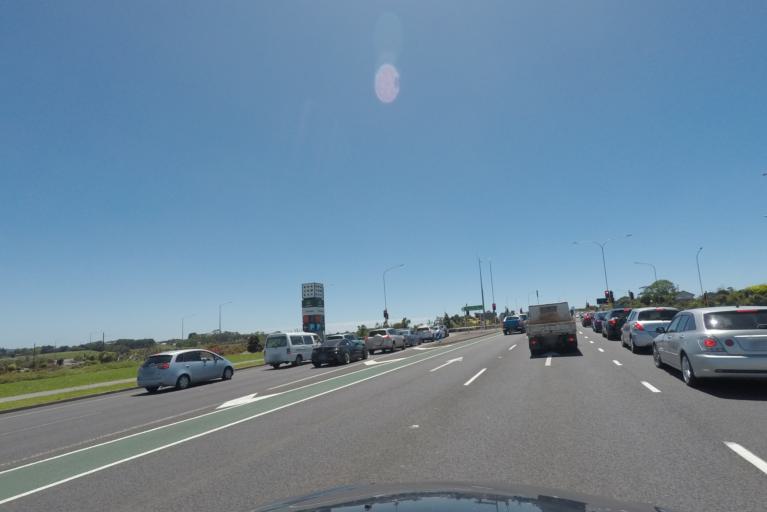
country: NZ
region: Auckland
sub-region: Auckland
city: Rosebank
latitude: -36.8194
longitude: 174.6123
